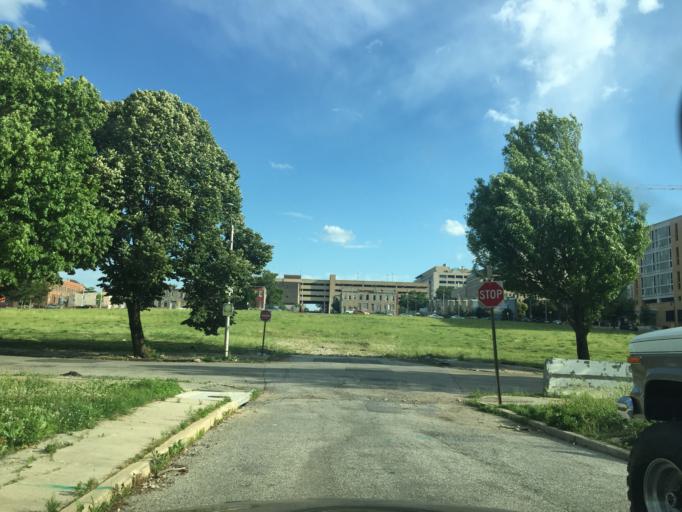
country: US
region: Maryland
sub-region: City of Baltimore
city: Baltimore
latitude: 39.3023
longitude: -76.5889
